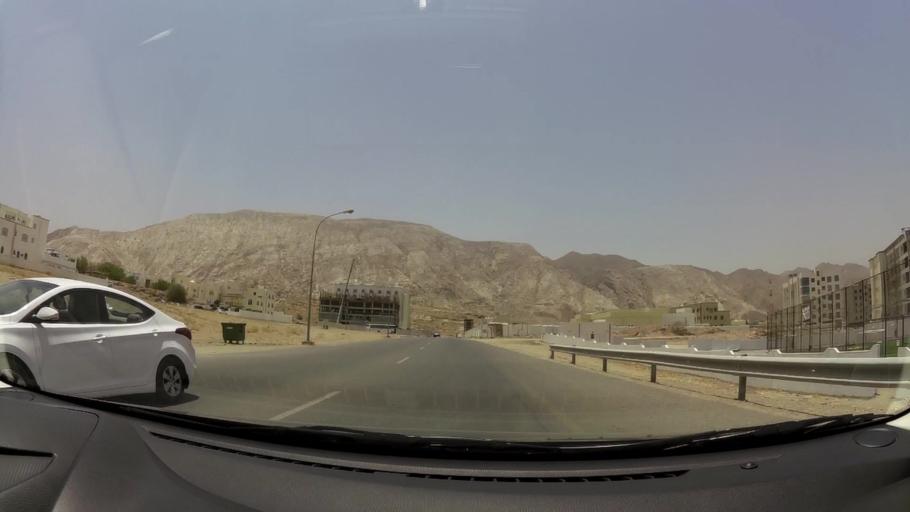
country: OM
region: Muhafazat Masqat
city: Bawshar
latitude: 23.5590
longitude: 58.4089
